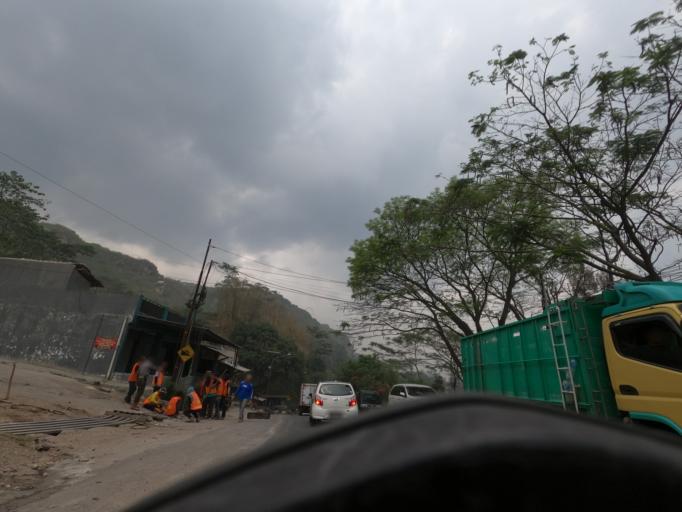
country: ID
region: West Java
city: Padalarang
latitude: -6.8322
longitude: 107.4478
